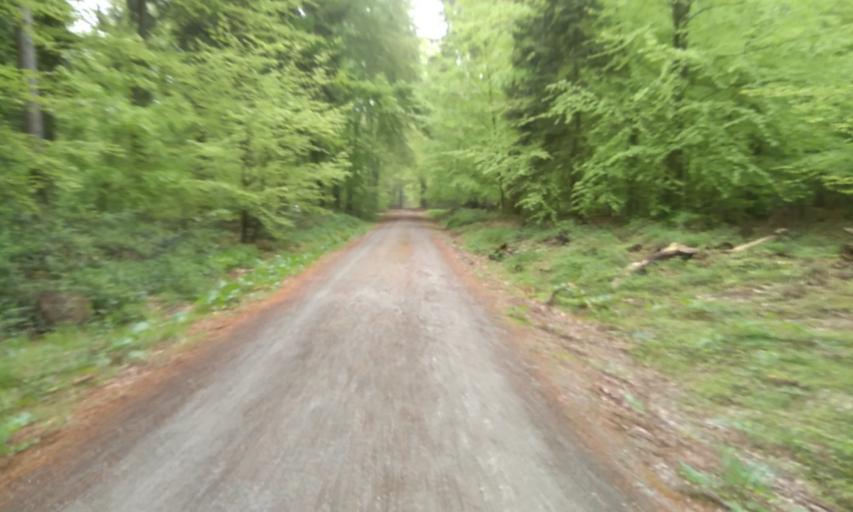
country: DE
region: Lower Saxony
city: Nottensdorf
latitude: 53.4716
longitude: 9.6378
